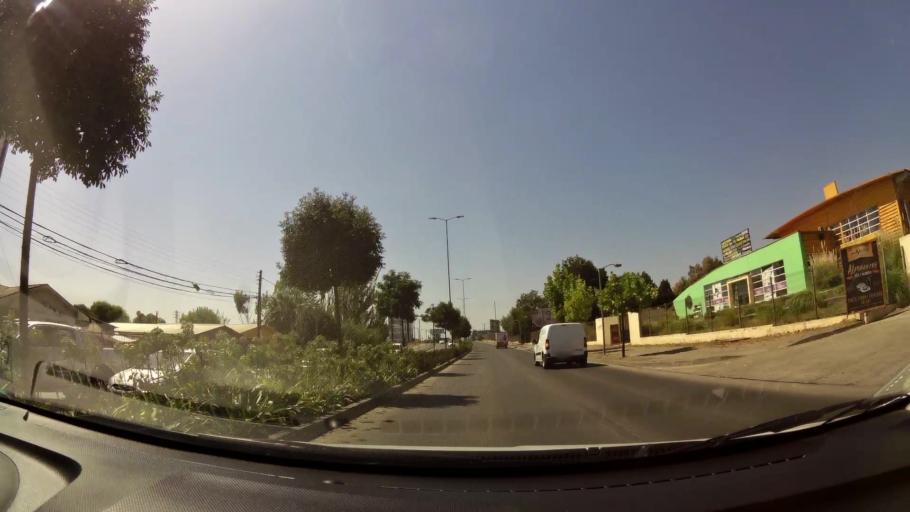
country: CL
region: Maule
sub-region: Provincia de Talca
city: Talca
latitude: -35.4284
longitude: -71.6383
